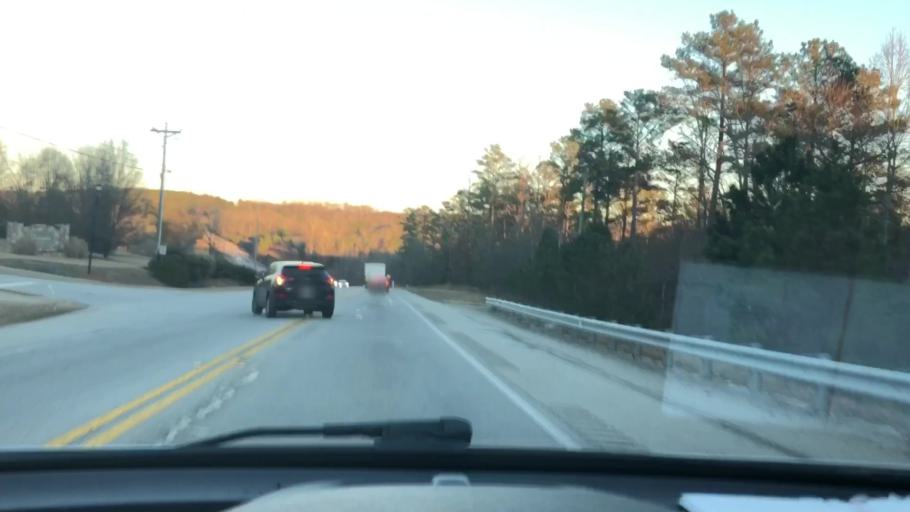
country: US
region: Georgia
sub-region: Walton County
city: Loganville
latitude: 33.8804
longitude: -83.8289
